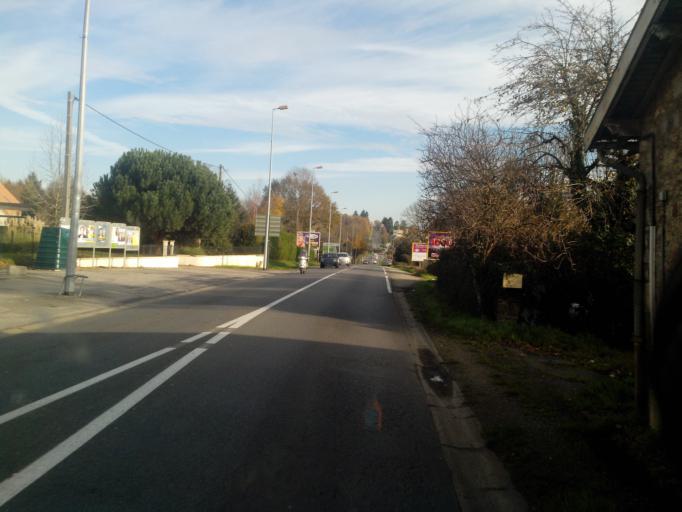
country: FR
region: Limousin
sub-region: Departement de la Haute-Vienne
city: Feytiat
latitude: 45.8154
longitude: 1.3146
